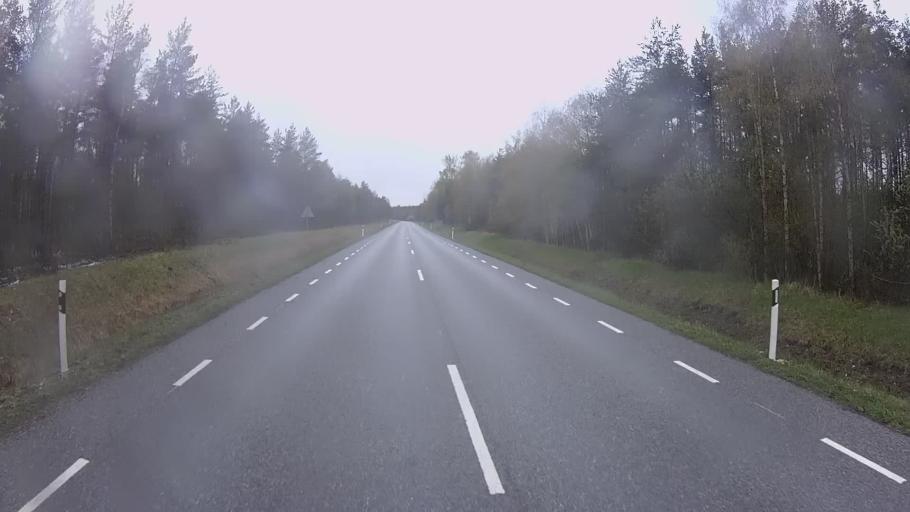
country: EE
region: Hiiumaa
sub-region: Kaerdla linn
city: Kardla
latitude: 59.0026
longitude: 22.5443
